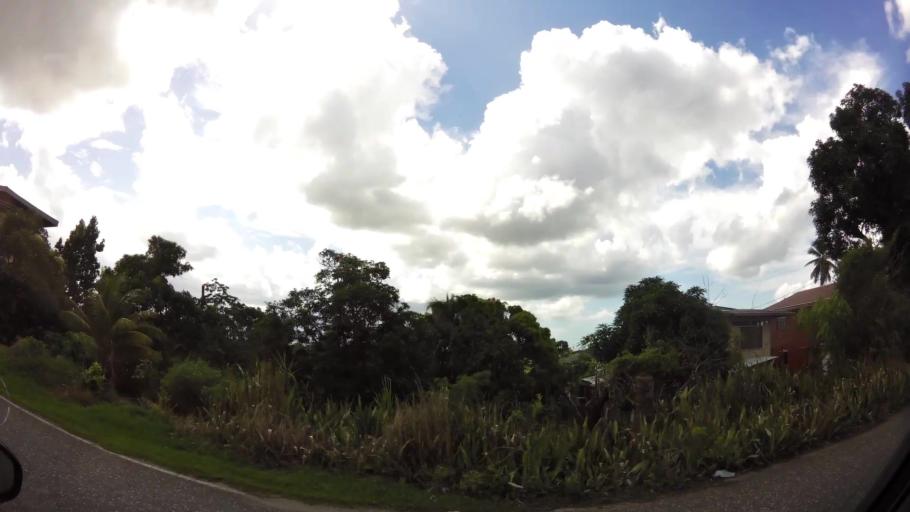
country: TT
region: Penal/Debe
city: Debe
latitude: 10.2318
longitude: -61.4409
